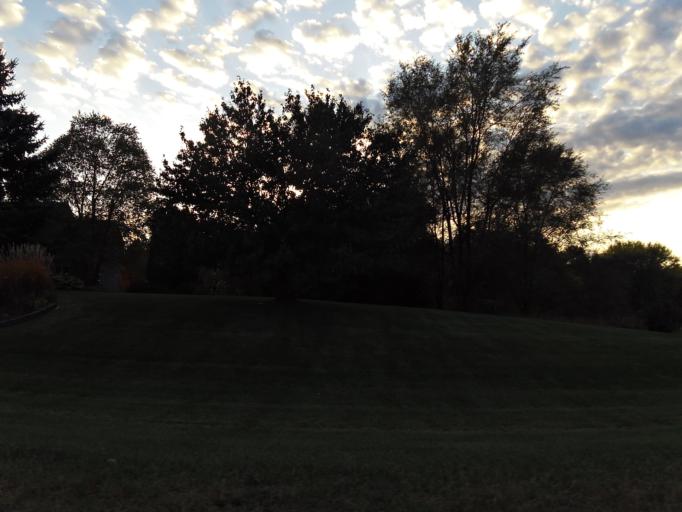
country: US
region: Minnesota
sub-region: Washington County
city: Lakeland
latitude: 44.9785
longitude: -92.8031
